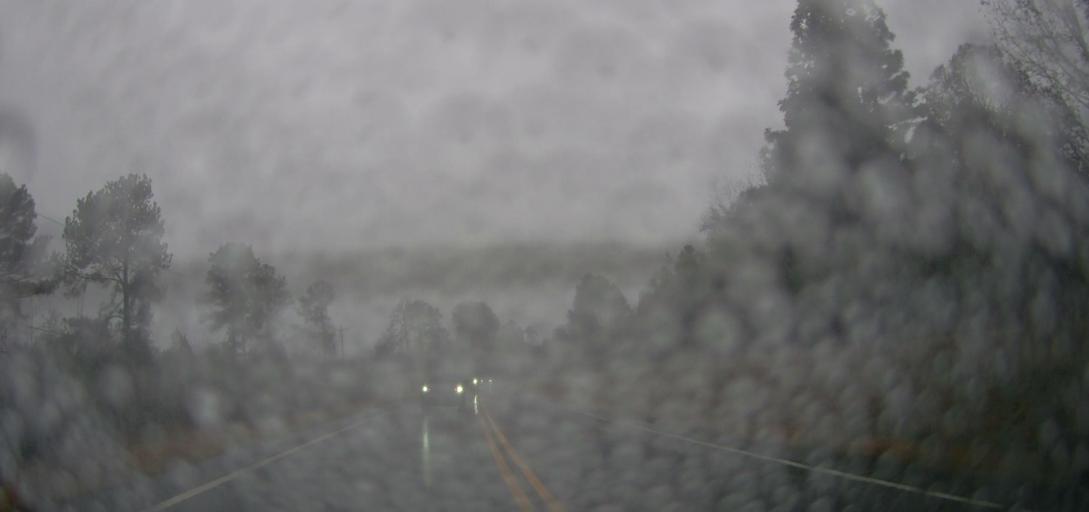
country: US
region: Georgia
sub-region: Putnam County
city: Eatonton
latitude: 33.2661
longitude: -83.4137
